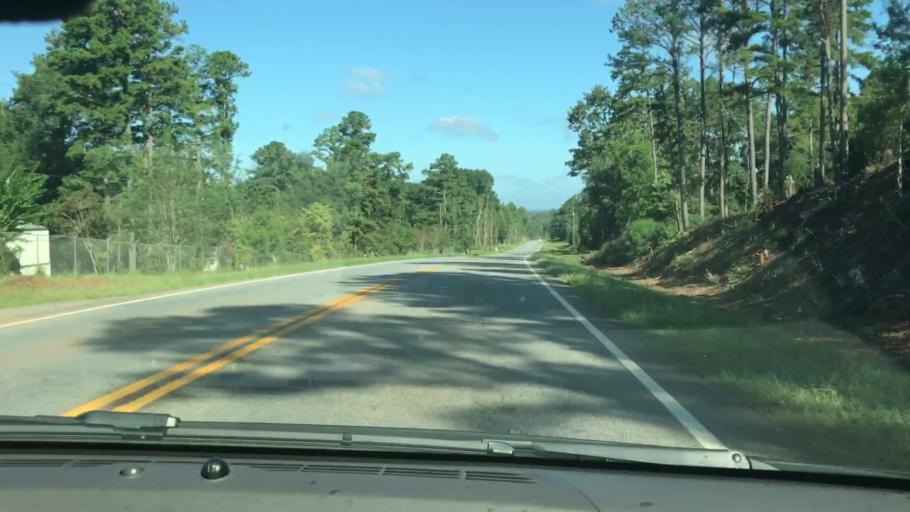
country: US
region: Georgia
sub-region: Quitman County
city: Georgetown
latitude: 31.8622
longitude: -85.0704
